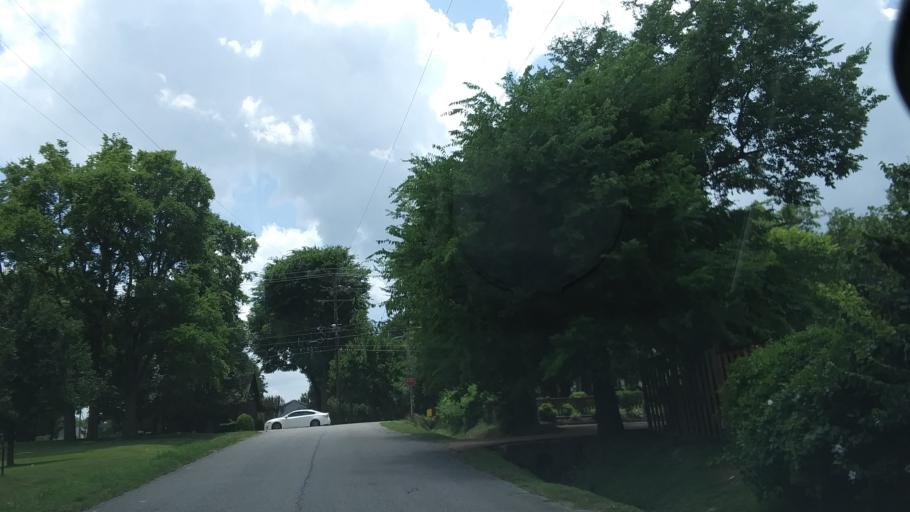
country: US
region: Tennessee
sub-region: Davidson County
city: Belle Meade
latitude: 36.1579
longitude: -86.8722
